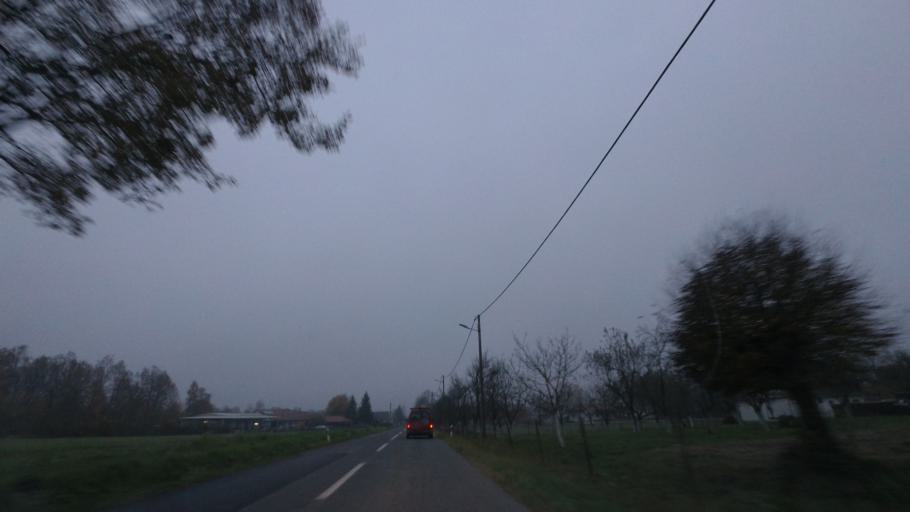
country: HR
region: Sisacko-Moslavacka
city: Petrinja
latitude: 45.4653
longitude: 16.2536
